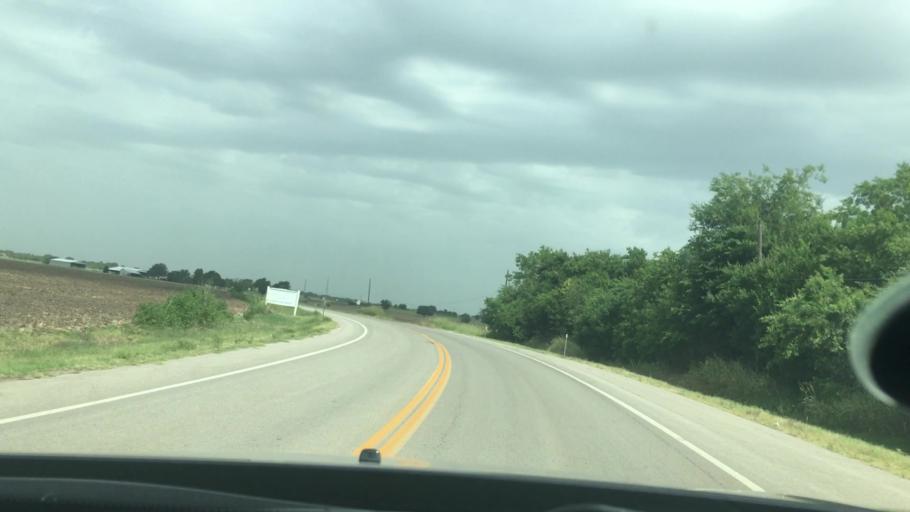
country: US
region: Oklahoma
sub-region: Garvin County
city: Pauls Valley
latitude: 34.8300
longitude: -97.2597
